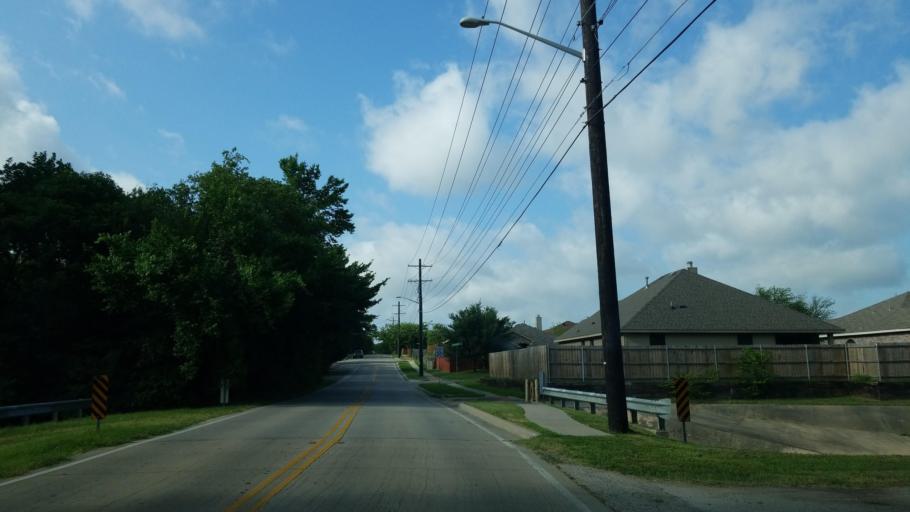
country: US
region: Texas
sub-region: Denton County
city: Denton
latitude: 33.2312
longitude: -97.0989
